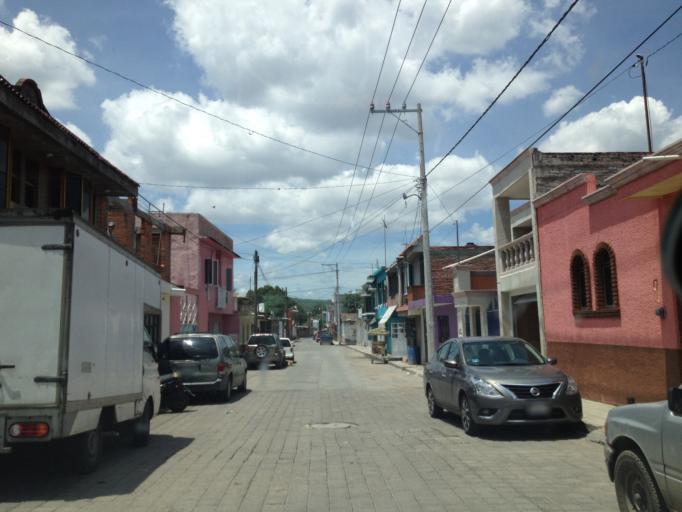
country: MX
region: Michoacan
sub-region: Tarimbaro
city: El Colegio
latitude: 19.7939
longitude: -101.1748
